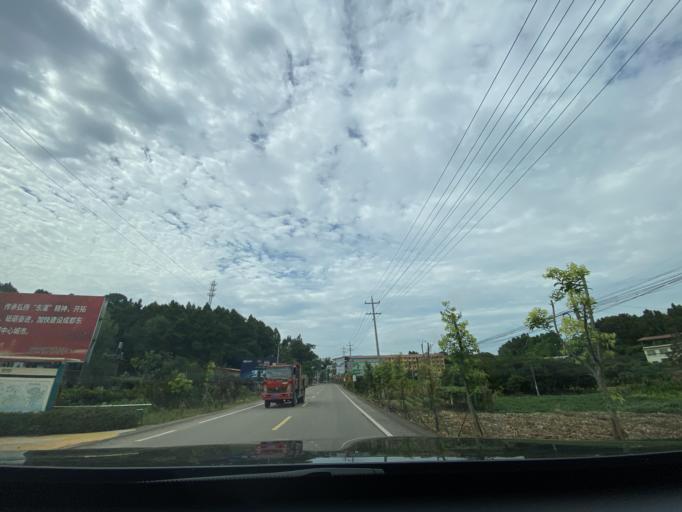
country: CN
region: Sichuan
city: Jiancheng
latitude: 30.4833
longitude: 104.6339
